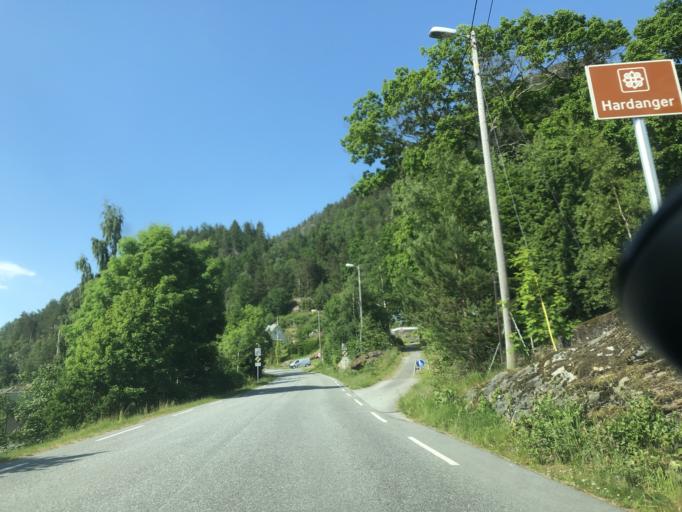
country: NO
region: Hordaland
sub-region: Jondal
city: Jondal
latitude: 60.2795
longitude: 6.2508
